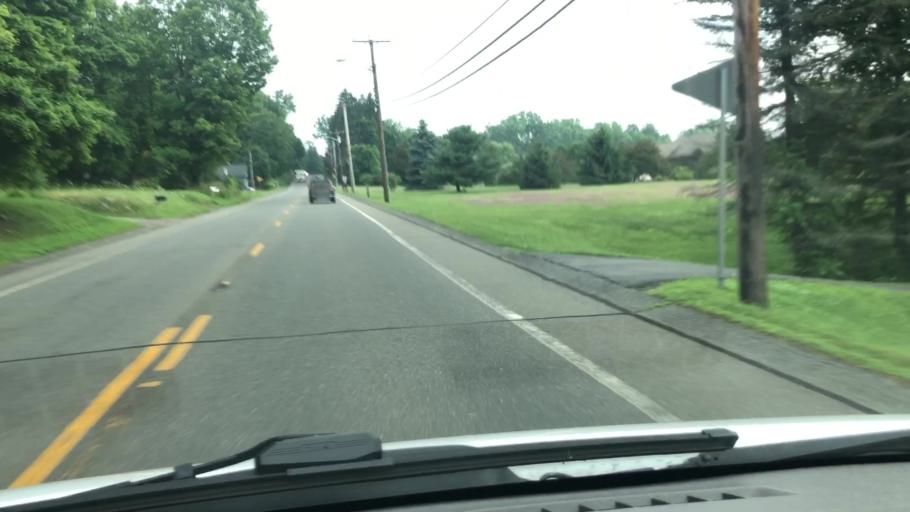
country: US
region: Massachusetts
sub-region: Berkshire County
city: Adams
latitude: 42.5719
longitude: -73.1543
